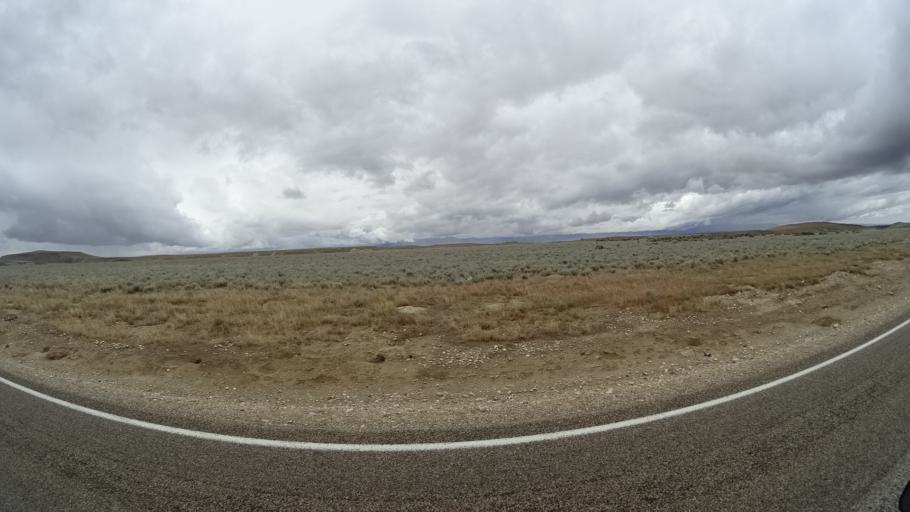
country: US
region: Idaho
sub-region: Owyhee County
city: Murphy
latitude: 43.2721
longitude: -116.3902
